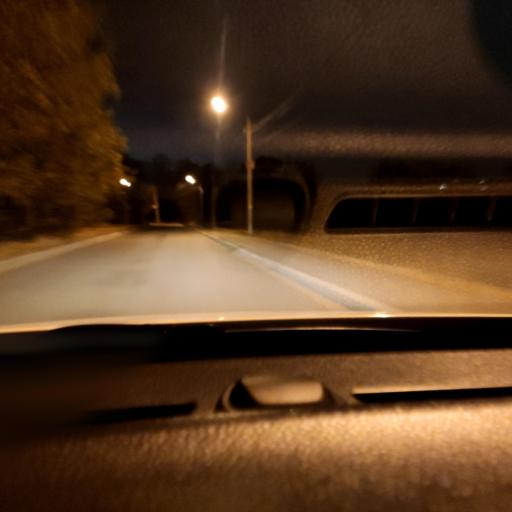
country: RU
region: Voronezj
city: Podgornoye
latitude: 51.7316
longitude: 39.1956
